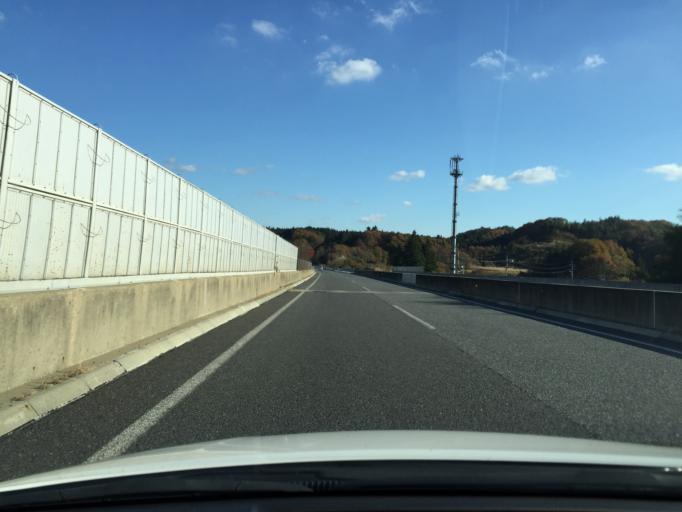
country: JP
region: Fukushima
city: Funehikimachi-funehiki
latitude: 37.2730
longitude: 140.6278
